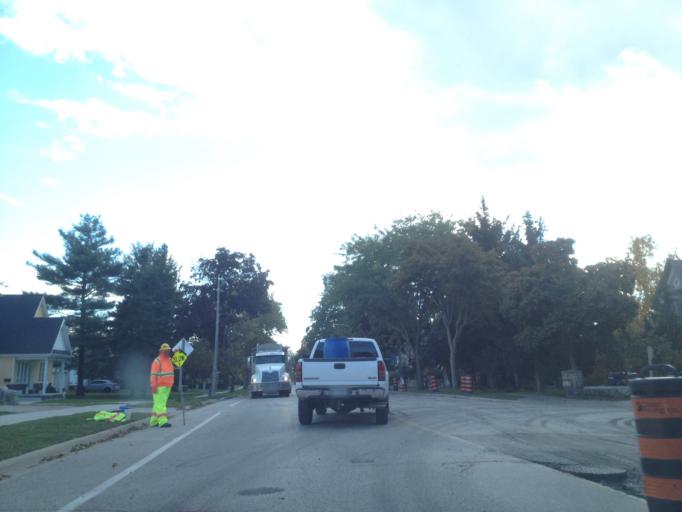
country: CA
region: Ontario
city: Amherstburg
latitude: 42.0328
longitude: -82.7399
